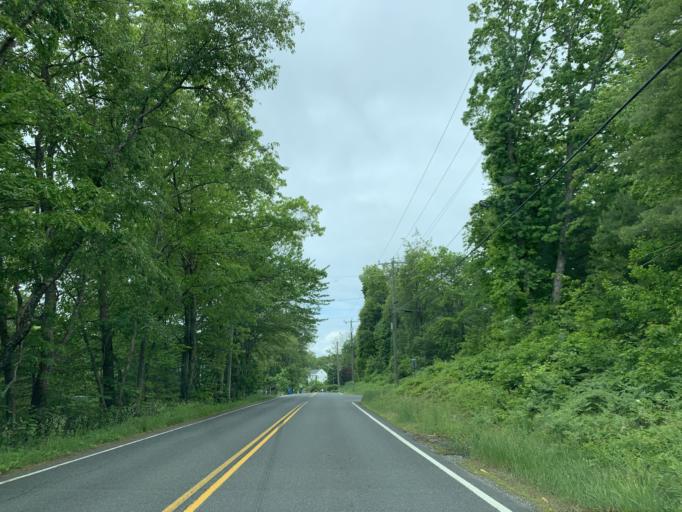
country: US
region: Massachusetts
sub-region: Hampshire County
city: Southampton
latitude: 42.2077
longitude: -72.8056
